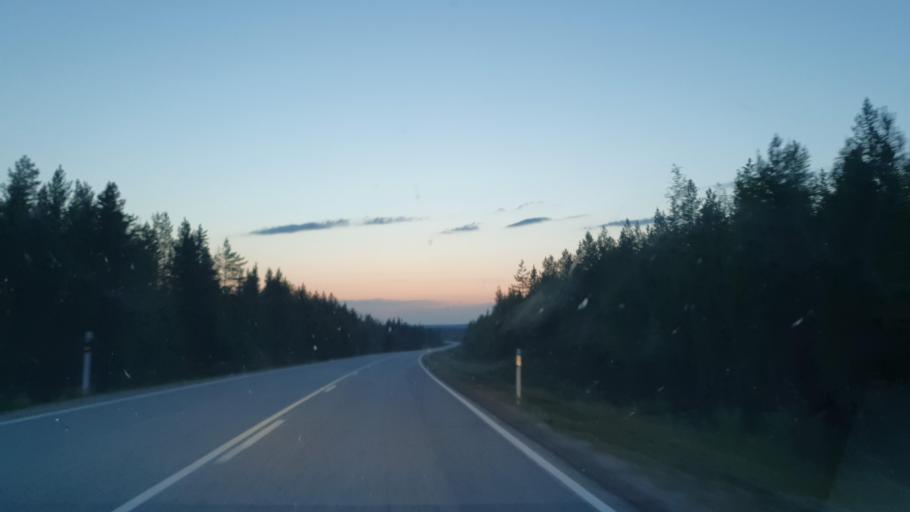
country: FI
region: Northern Ostrobothnia
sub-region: Koillismaa
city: Kuusamo
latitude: 65.4858
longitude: 28.9485
